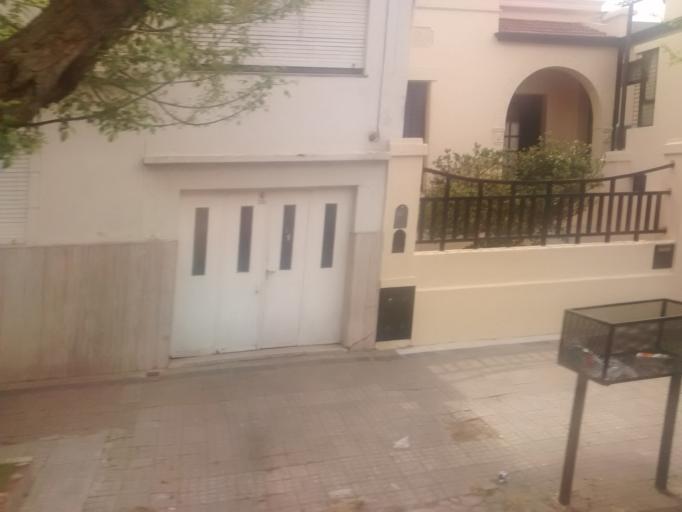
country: AR
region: Buenos Aires
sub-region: Partido de La Plata
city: La Plata
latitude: -34.9263
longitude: -57.9290
